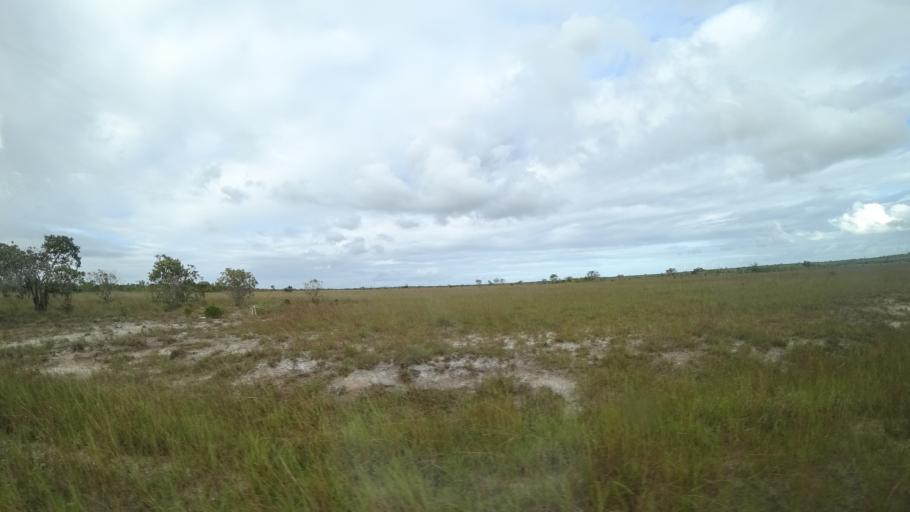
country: MZ
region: Sofala
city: Beira
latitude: -19.6234
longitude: 35.0606
